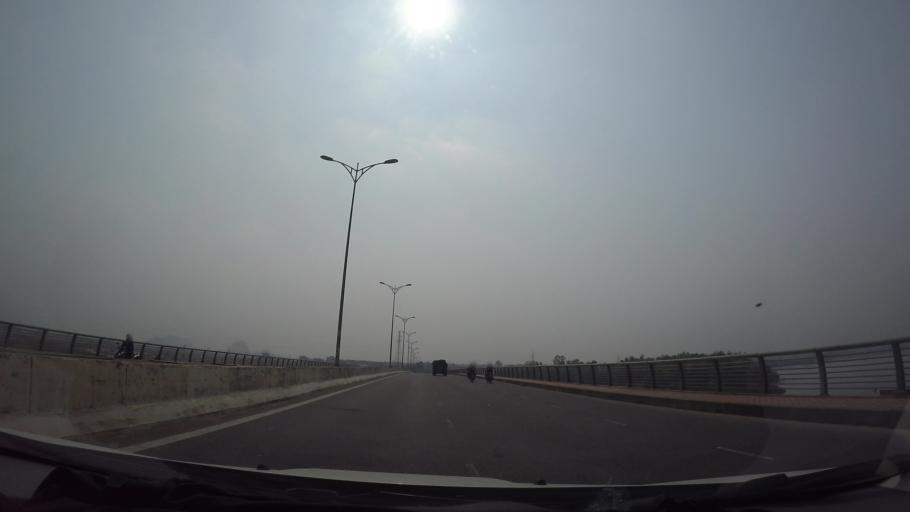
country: VN
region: Da Nang
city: Ngu Hanh Son
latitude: 16.0014
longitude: 108.2293
